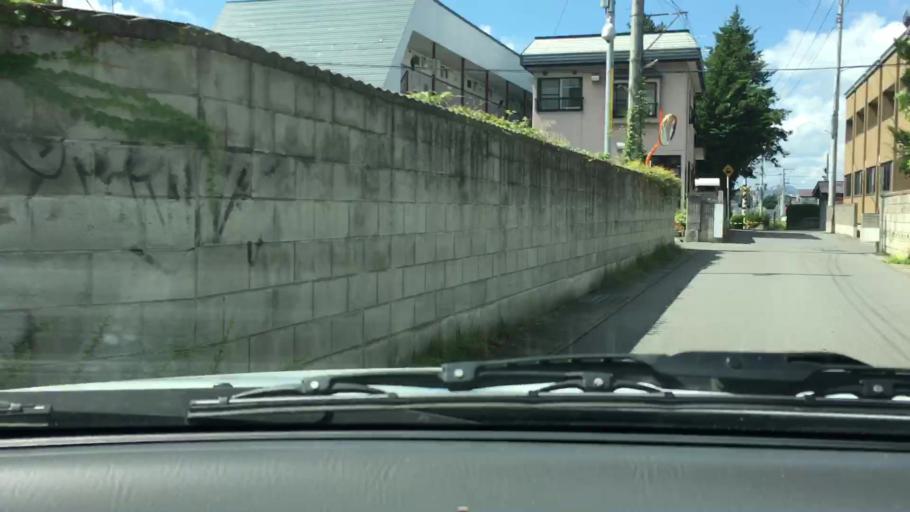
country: JP
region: Aomori
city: Hirosaki
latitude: 40.5881
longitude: 140.4701
